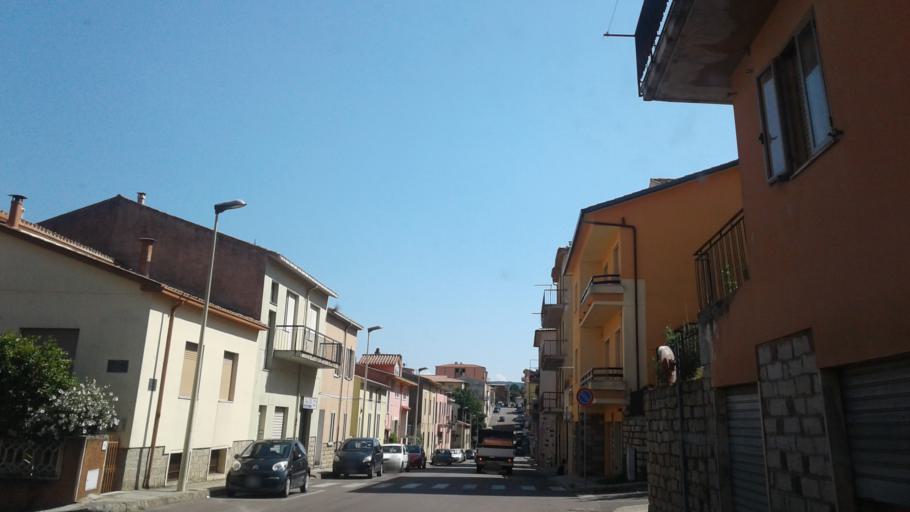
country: IT
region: Sardinia
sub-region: Provincia di Olbia-Tempio
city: Tempio Pausania
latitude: 40.9002
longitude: 9.1086
